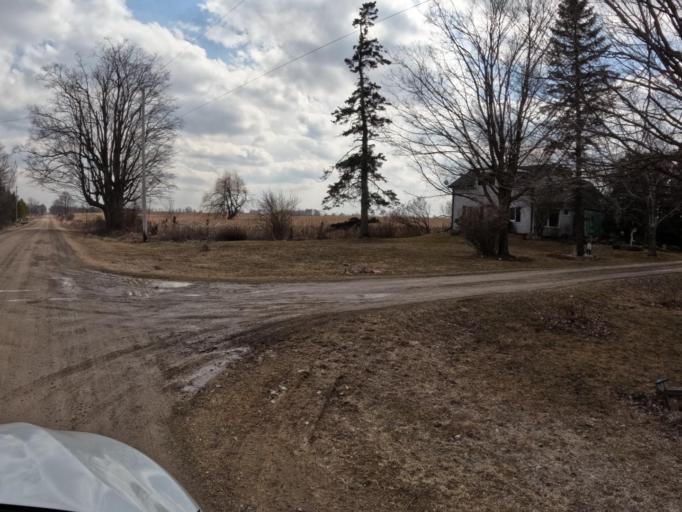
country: CA
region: Ontario
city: Shelburne
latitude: 43.9618
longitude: -80.2820
